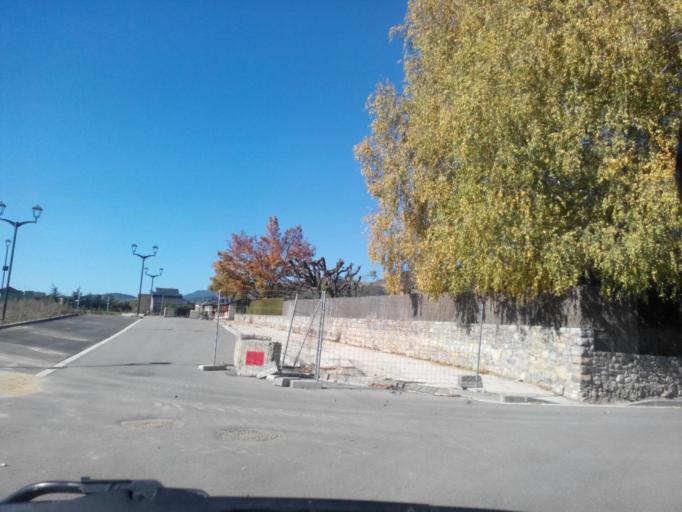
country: ES
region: Catalonia
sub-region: Provincia de Lleida
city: Bellver de Cerdanya
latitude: 42.3681
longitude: 1.7799
